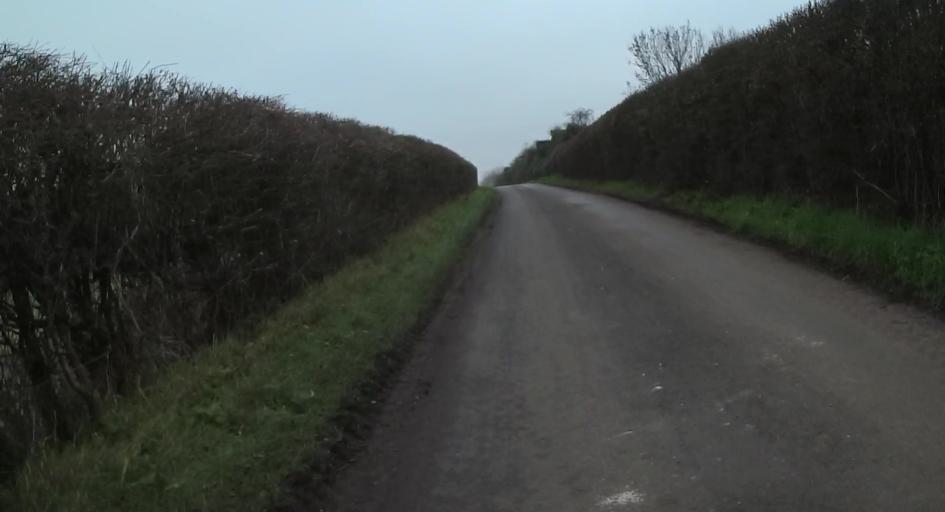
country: GB
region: England
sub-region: Hampshire
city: Kings Worthy
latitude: 51.1136
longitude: -1.2114
